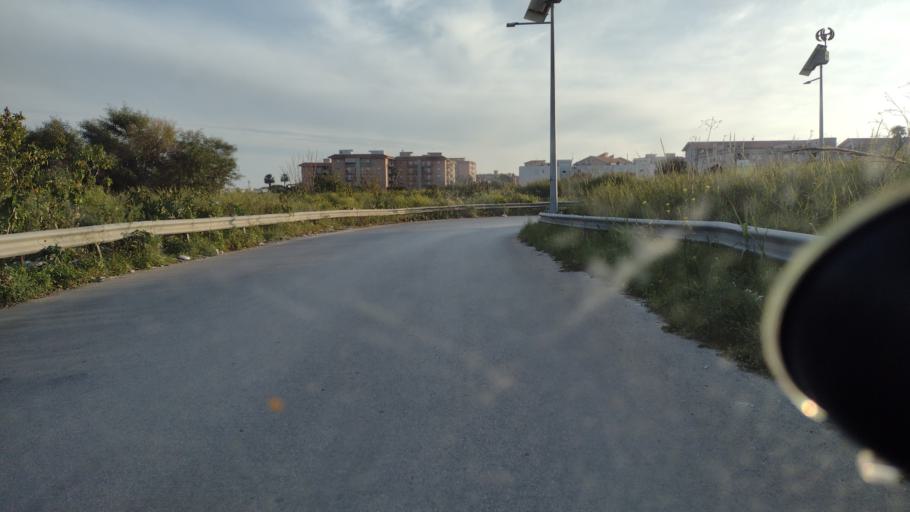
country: IT
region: Sicily
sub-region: Provincia di Siracusa
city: Avola
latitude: 36.9204
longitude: 15.1425
